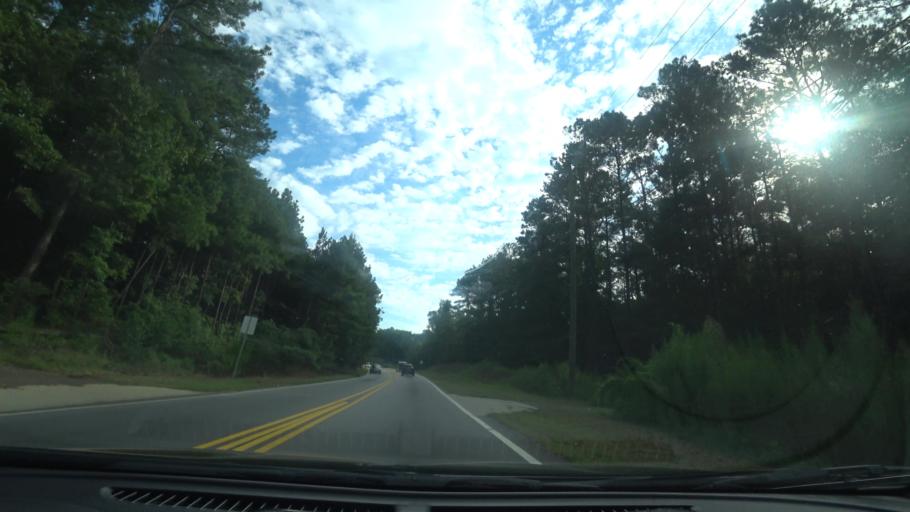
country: US
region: Georgia
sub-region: Rockdale County
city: Conyers
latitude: 33.6435
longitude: -83.9745
